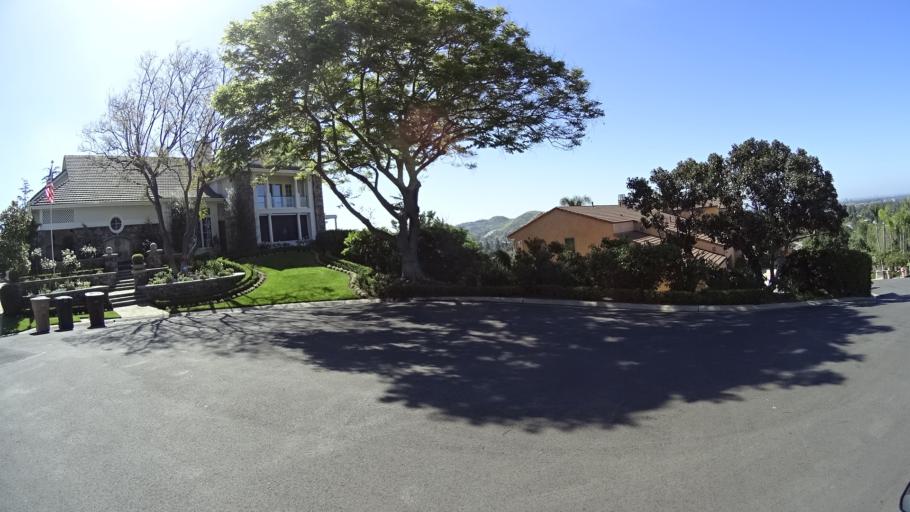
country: US
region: California
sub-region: Orange County
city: Villa Park
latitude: 33.8211
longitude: -117.8023
